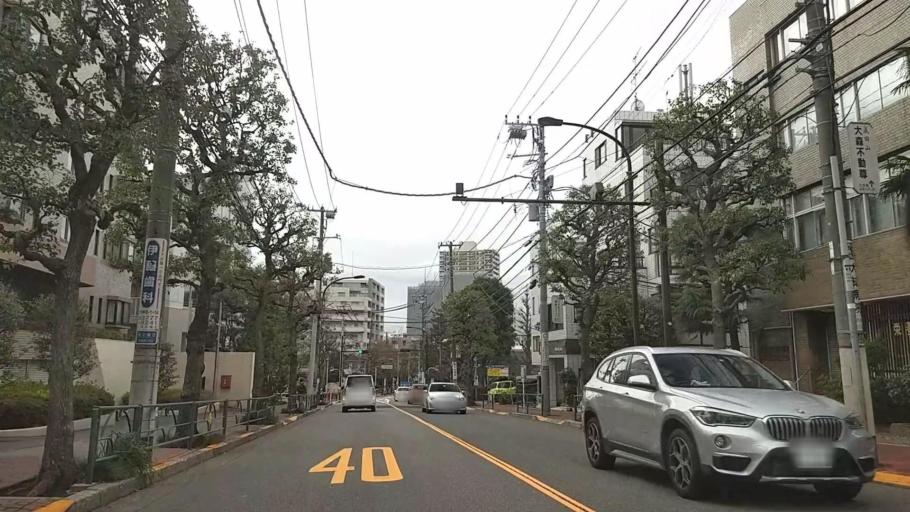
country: JP
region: Kanagawa
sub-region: Kawasaki-shi
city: Kawasaki
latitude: 35.5946
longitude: 139.7297
